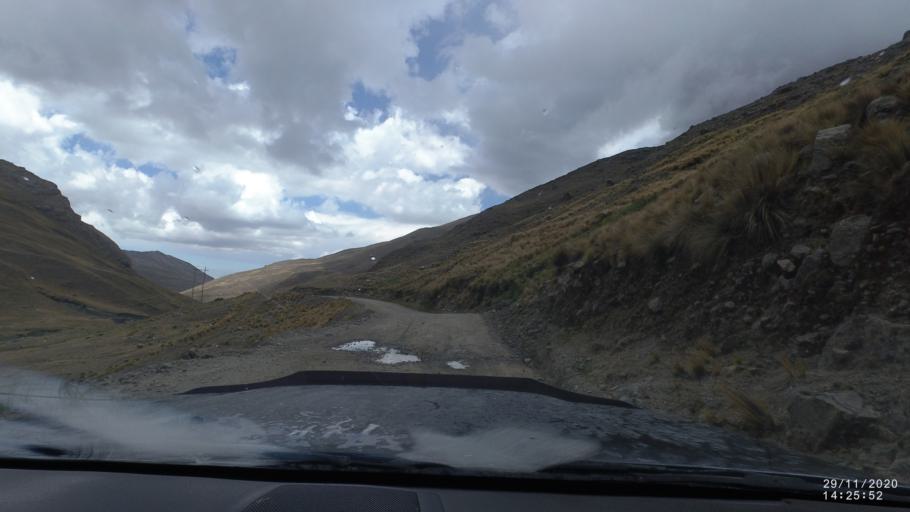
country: BO
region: Cochabamba
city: Sipe Sipe
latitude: -17.2556
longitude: -66.3738
